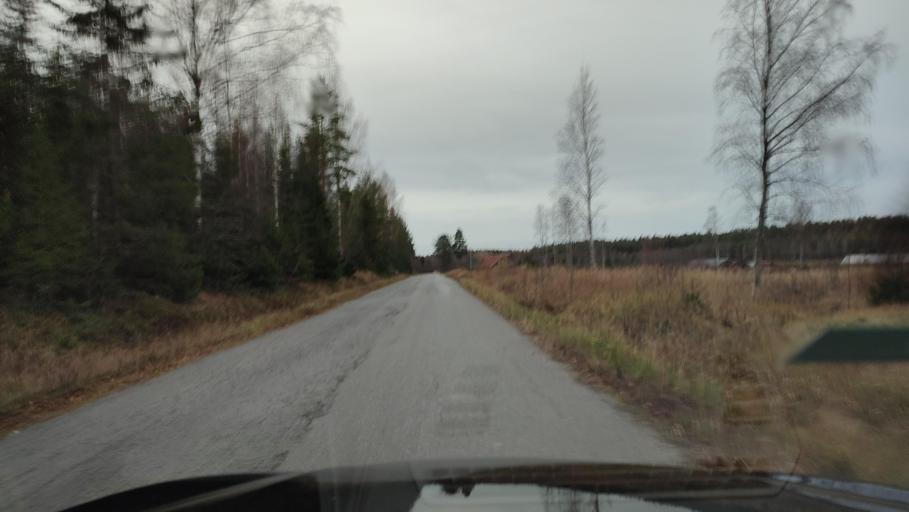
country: FI
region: Ostrobothnia
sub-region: Sydosterbotten
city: Naerpes
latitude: 62.4234
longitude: 21.4106
